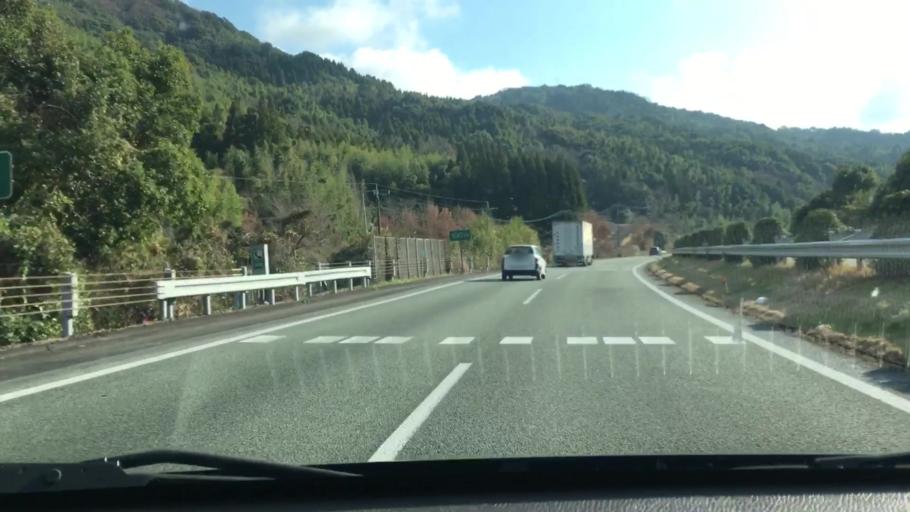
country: JP
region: Kumamoto
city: Matsubase
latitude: 32.6137
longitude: 130.7241
